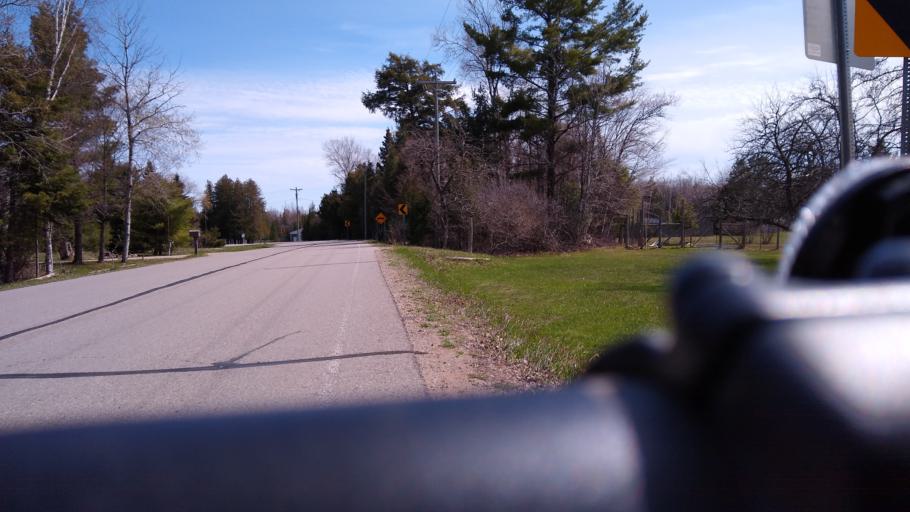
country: US
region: Michigan
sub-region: Delta County
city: Escanaba
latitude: 45.6878
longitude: -87.1525
